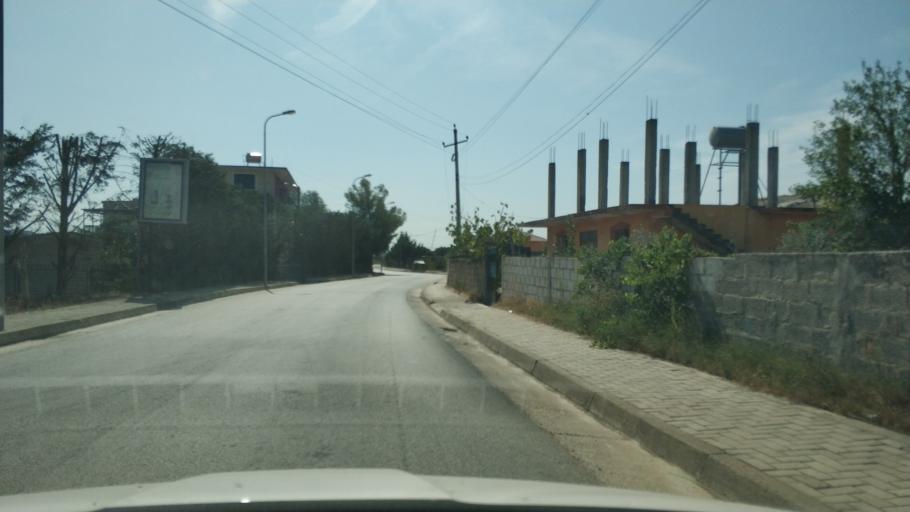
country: AL
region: Fier
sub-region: Rrethi i Lushnjes
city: Divjake
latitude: 40.9885
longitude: 19.5344
